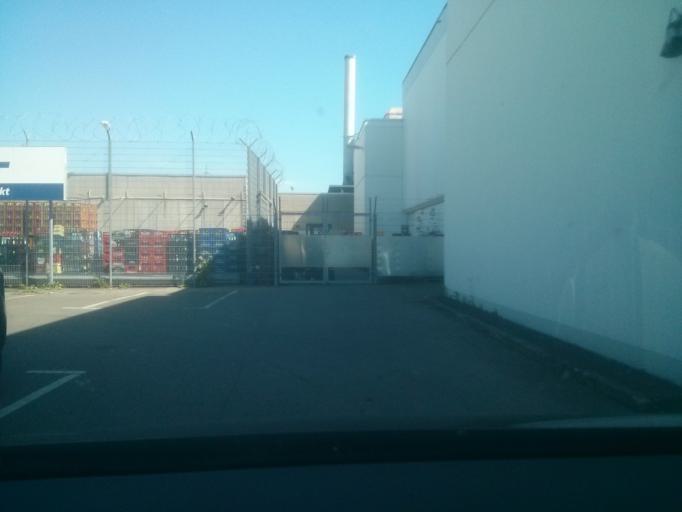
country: DE
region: Baden-Wuerttemberg
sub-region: Tuebingen Region
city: Wannweil
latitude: 48.4965
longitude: 9.1570
